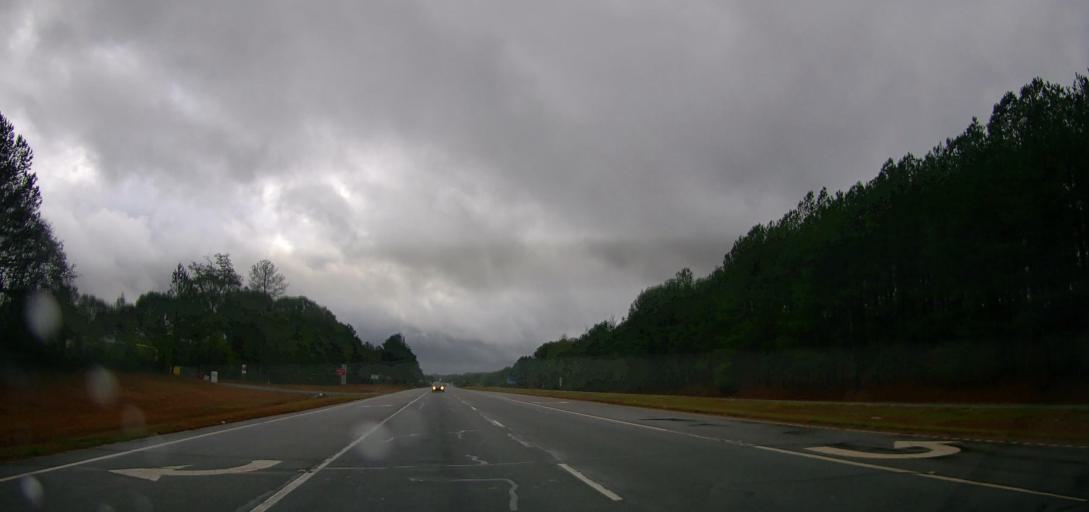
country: US
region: Georgia
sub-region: Oconee County
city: Watkinsville
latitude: 33.8805
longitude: -83.4152
